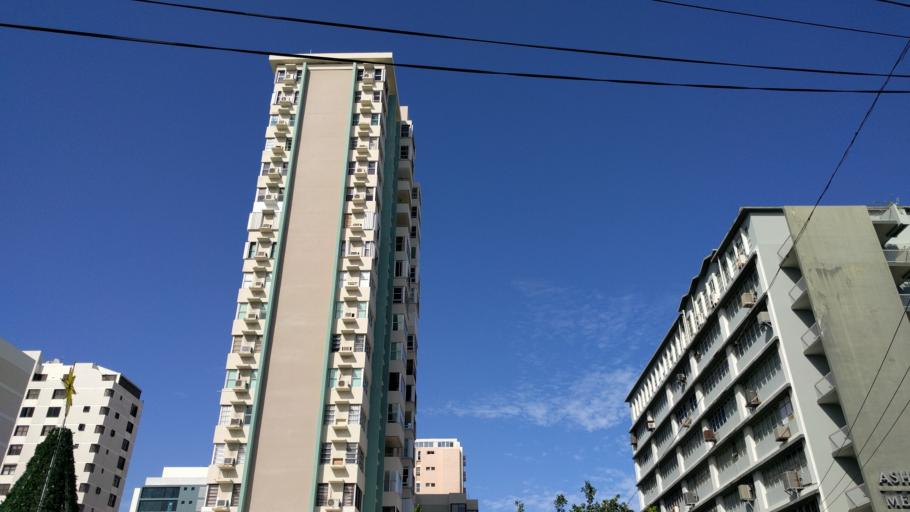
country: PR
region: San Juan
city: San Juan
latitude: 18.4547
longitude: -66.0663
